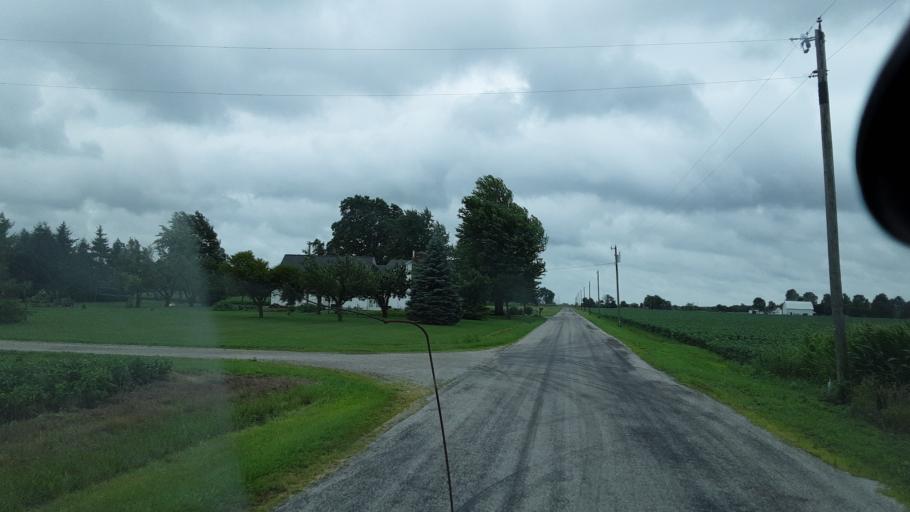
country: US
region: Indiana
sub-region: Wells County
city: Bluffton
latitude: 40.7921
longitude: -85.0717
